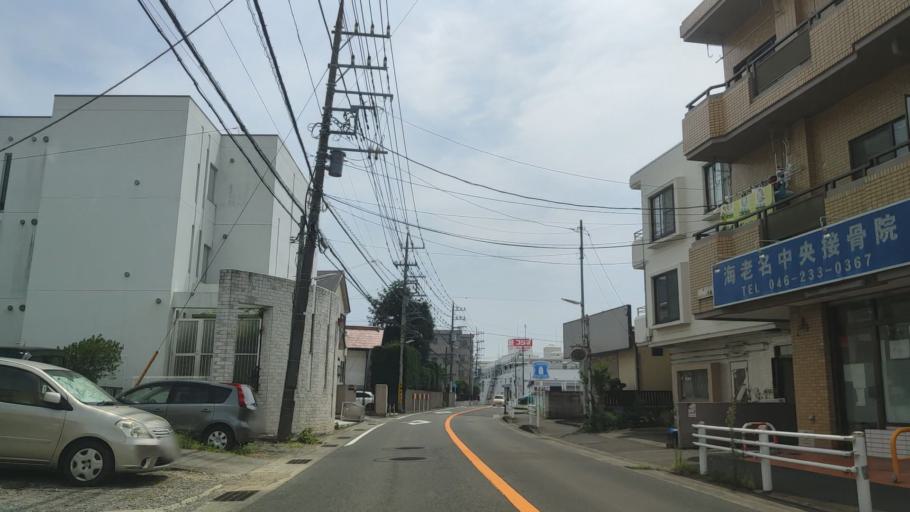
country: JP
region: Kanagawa
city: Atsugi
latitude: 35.4478
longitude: 139.3957
